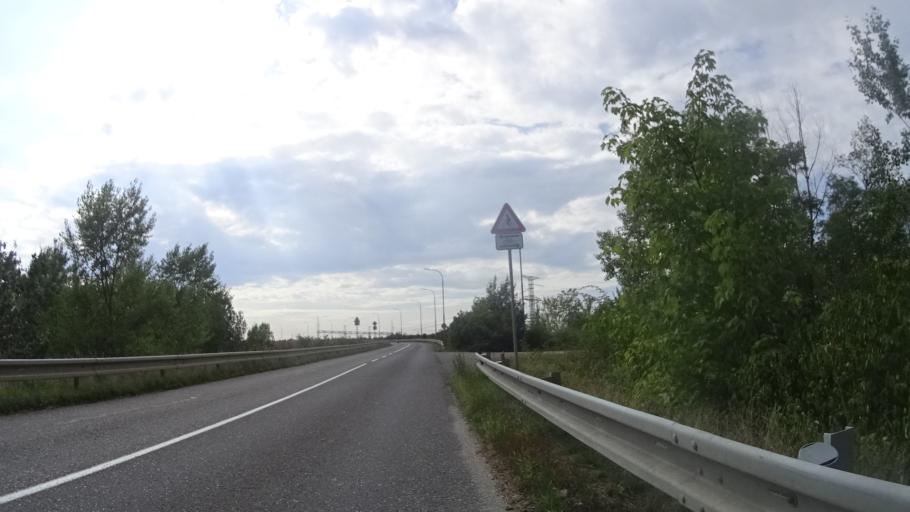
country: SK
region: Trnavsky
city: Gabcikovo
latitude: 47.8832
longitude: 17.5471
